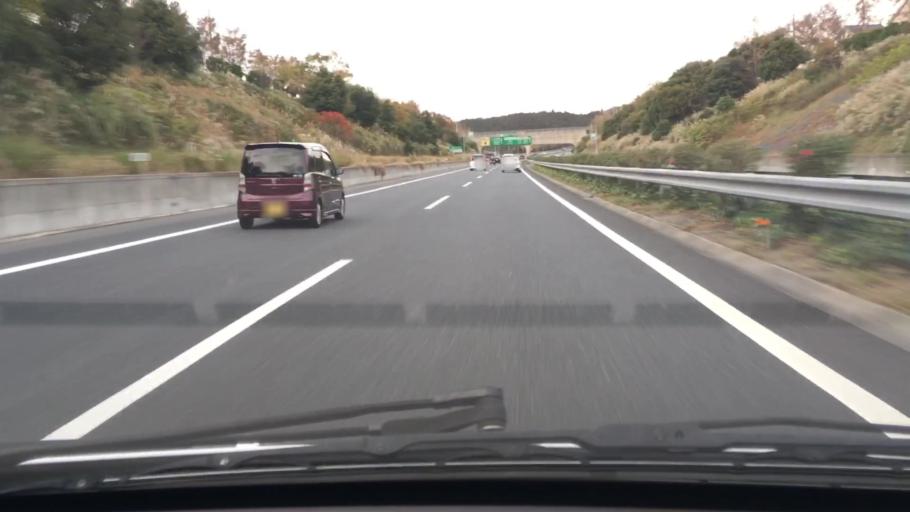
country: JP
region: Chiba
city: Kisarazu
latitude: 35.3431
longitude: 139.9442
